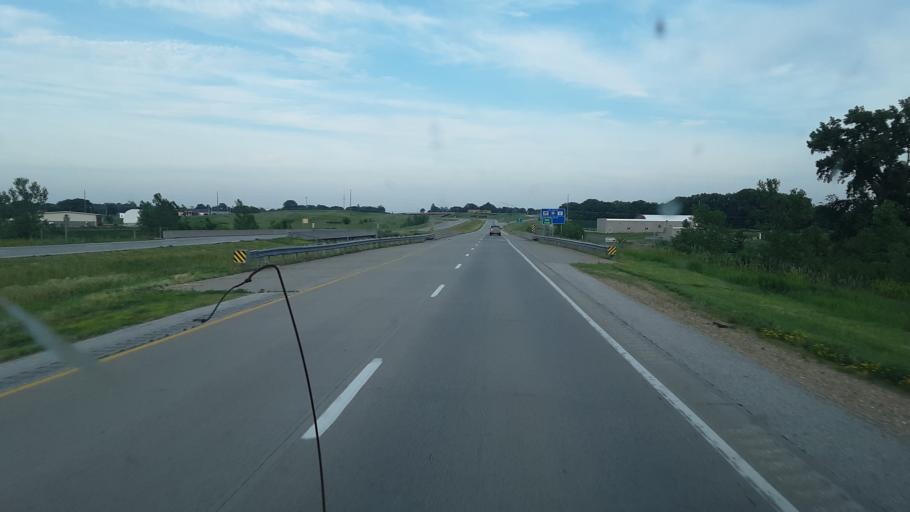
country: US
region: Iowa
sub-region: Tama County
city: Toledo
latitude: 41.9839
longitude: -92.5958
